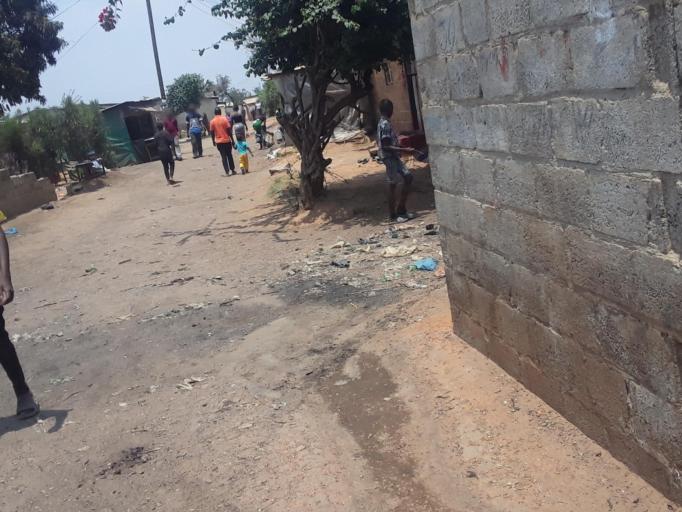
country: ZM
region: Lusaka
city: Lusaka
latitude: -15.3638
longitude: 28.2999
